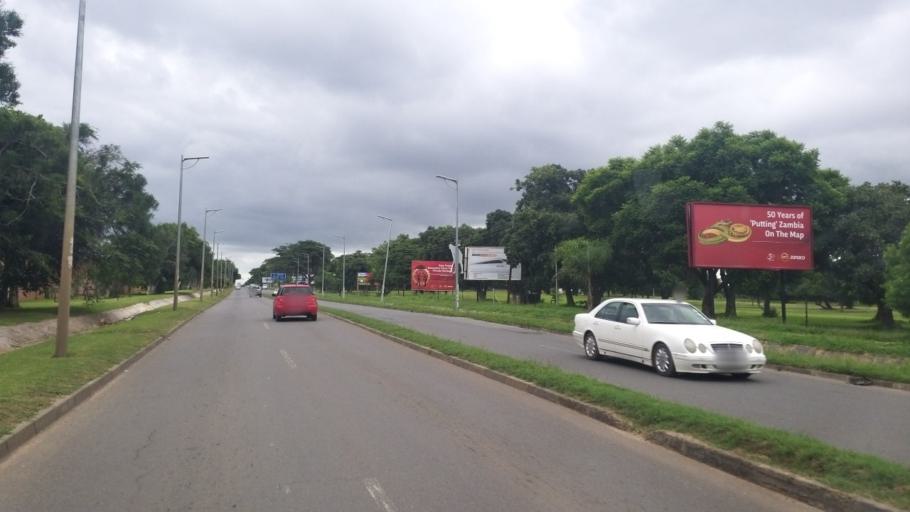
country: ZM
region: Lusaka
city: Lusaka
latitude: -15.4238
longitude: 28.3267
